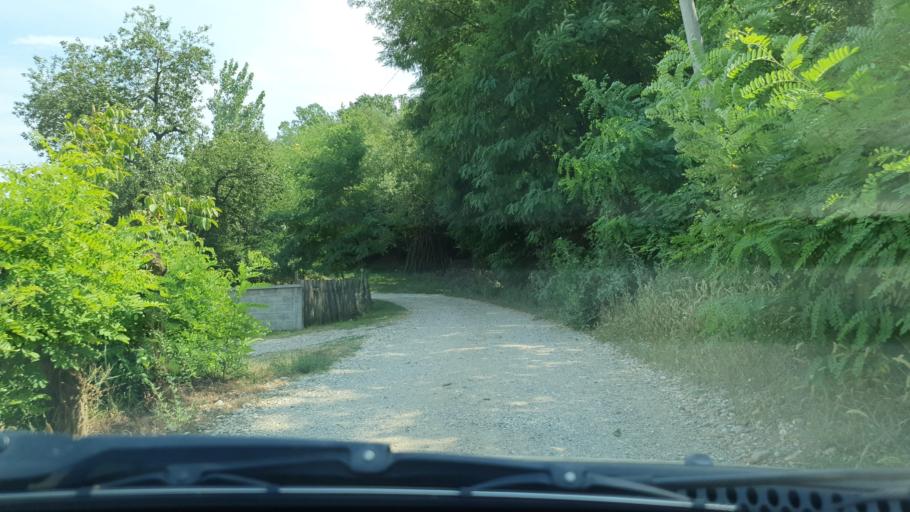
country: BA
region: Republika Srpska
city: Bijeljina
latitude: 44.7226
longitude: 19.1905
